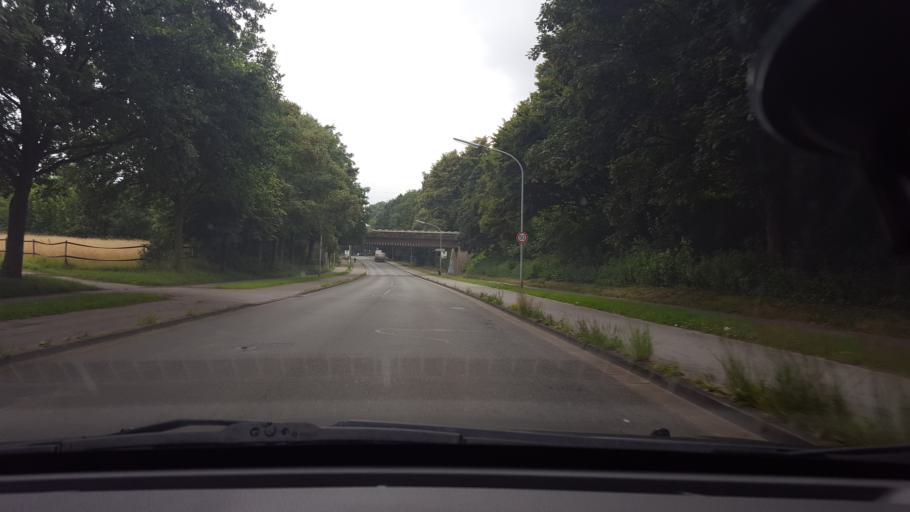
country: DE
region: North Rhine-Westphalia
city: Marl
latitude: 51.6117
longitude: 7.0682
